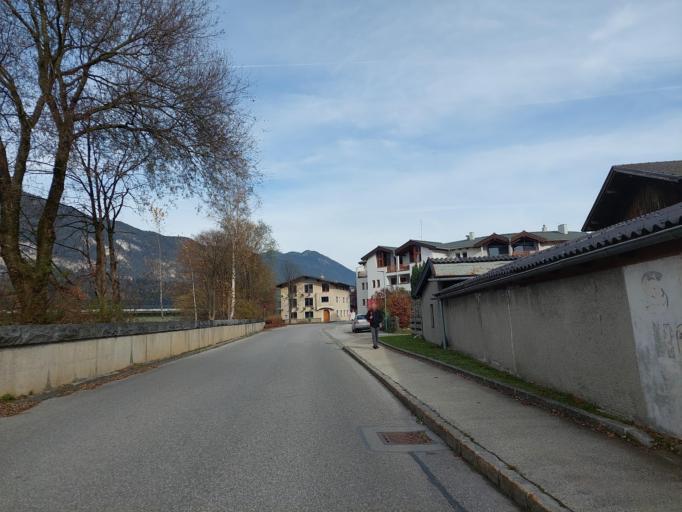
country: AT
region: Tyrol
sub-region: Politischer Bezirk Kufstein
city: Rattenberg
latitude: 47.4424
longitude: 11.8952
